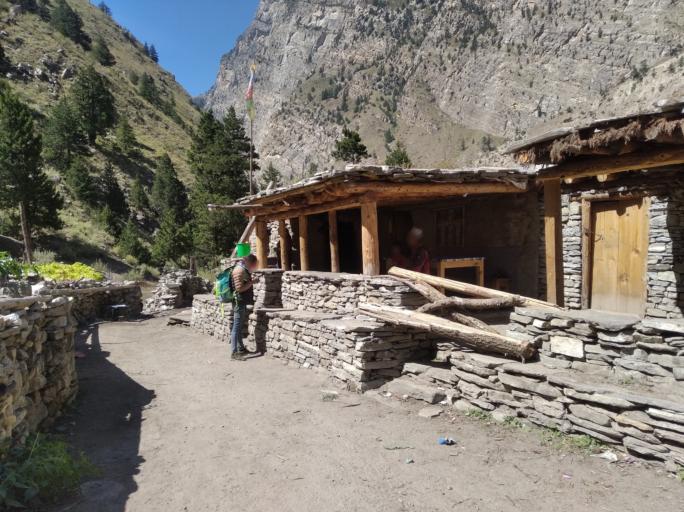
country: NP
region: Western Region
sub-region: Dhawalagiri Zone
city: Jomsom
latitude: 28.8942
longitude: 83.0690
